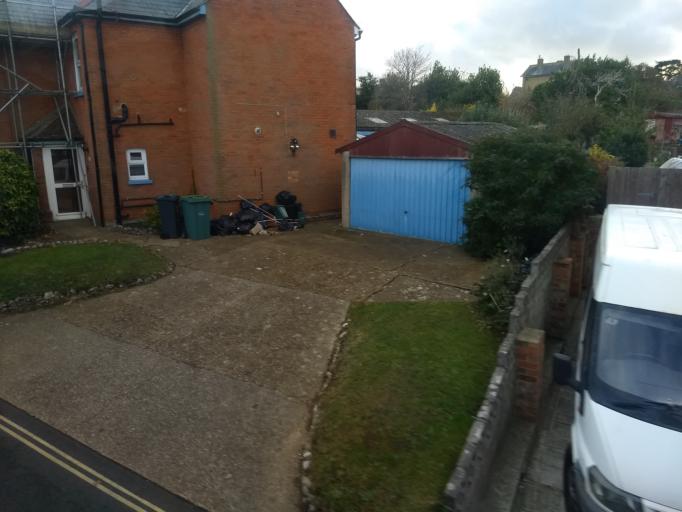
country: GB
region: England
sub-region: Isle of Wight
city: Newport
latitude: 50.6926
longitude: -1.3157
